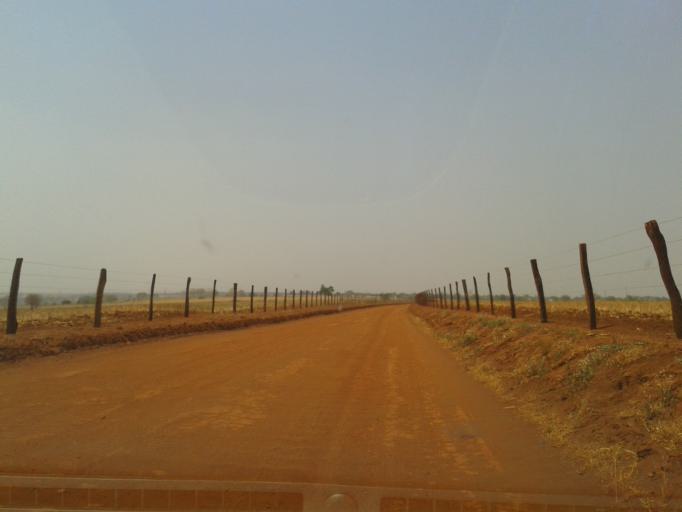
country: BR
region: Minas Gerais
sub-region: Centralina
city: Centralina
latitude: -18.7136
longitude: -49.2244
